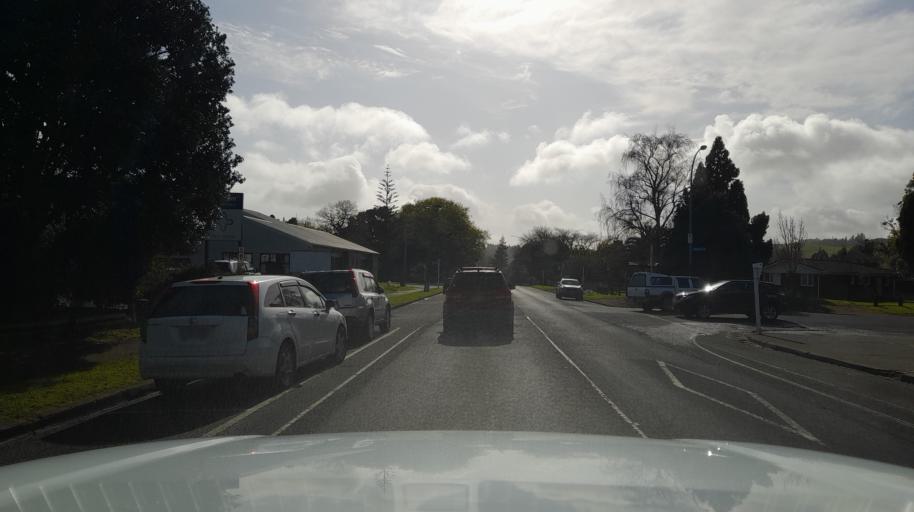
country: NZ
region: Northland
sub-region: Far North District
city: Waimate North
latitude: -35.4052
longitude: 173.8046
